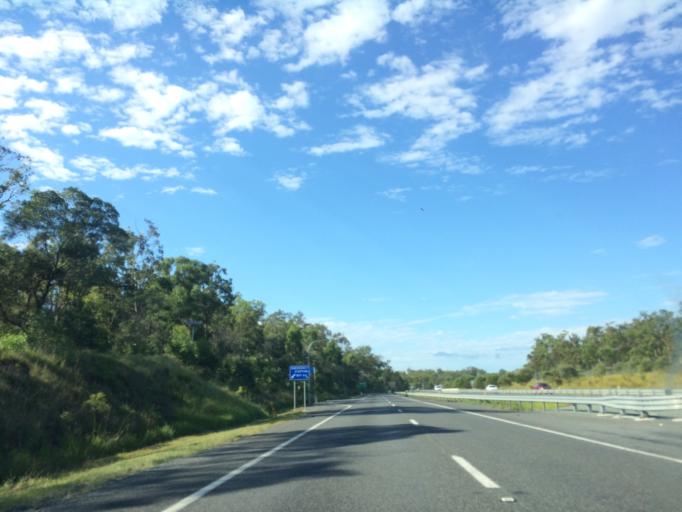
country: AU
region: Queensland
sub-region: Ipswich
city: Springfield
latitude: -27.6374
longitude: 152.9392
